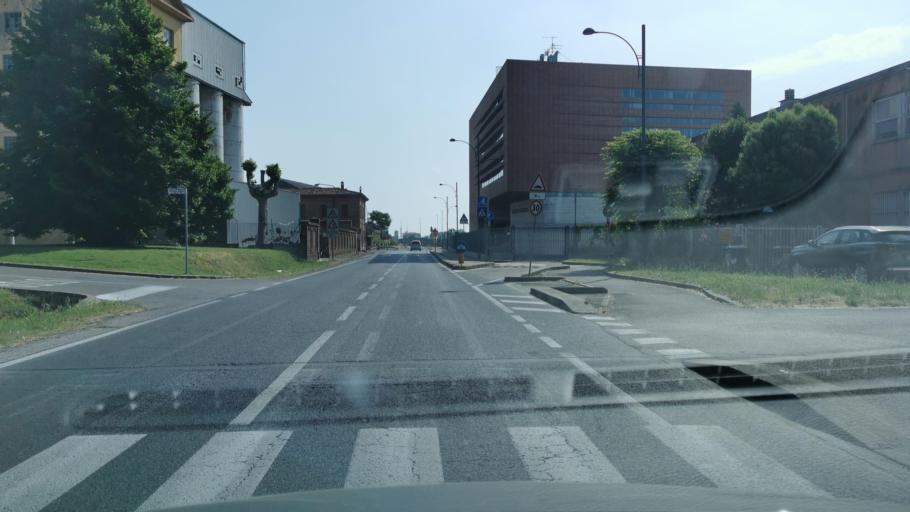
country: IT
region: Emilia-Romagna
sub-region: Provincia di Ravenna
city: Ravenna
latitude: 44.4224
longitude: 12.2115
